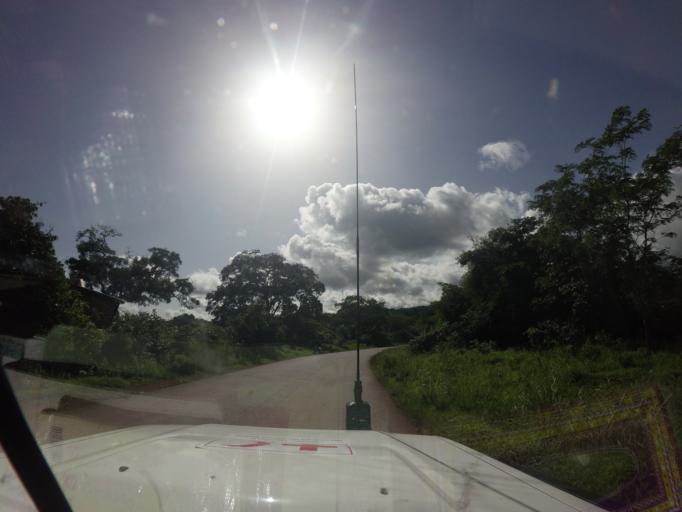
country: GN
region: Mamou
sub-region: Mamou Prefecture
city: Mamou
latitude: 10.3175
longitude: -12.2493
